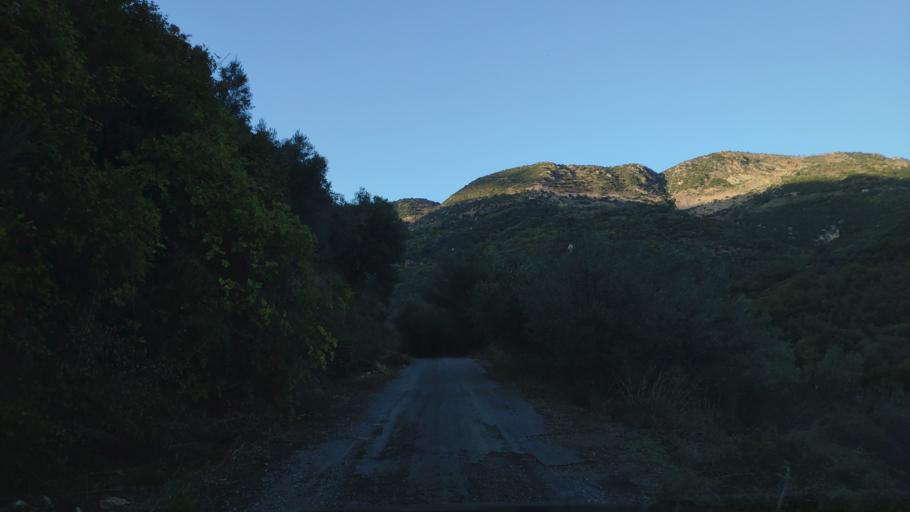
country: GR
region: Peloponnese
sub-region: Nomos Arkadias
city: Dimitsana
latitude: 37.5700
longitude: 22.0422
